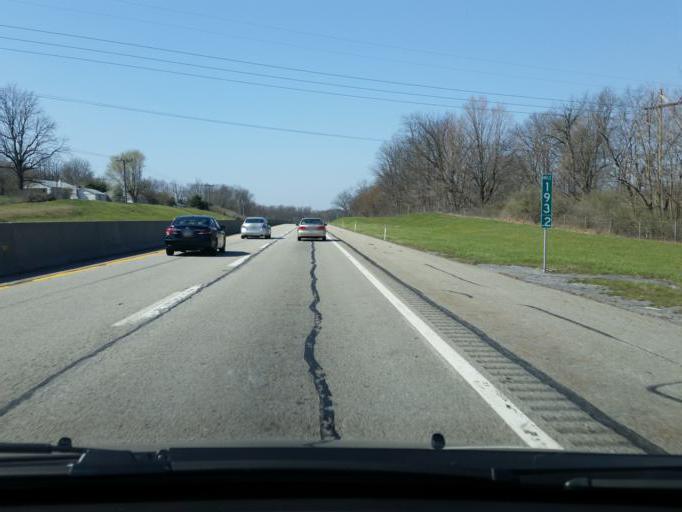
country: US
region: Pennsylvania
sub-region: Franklin County
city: Doylestown
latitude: 40.1323
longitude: -77.7402
